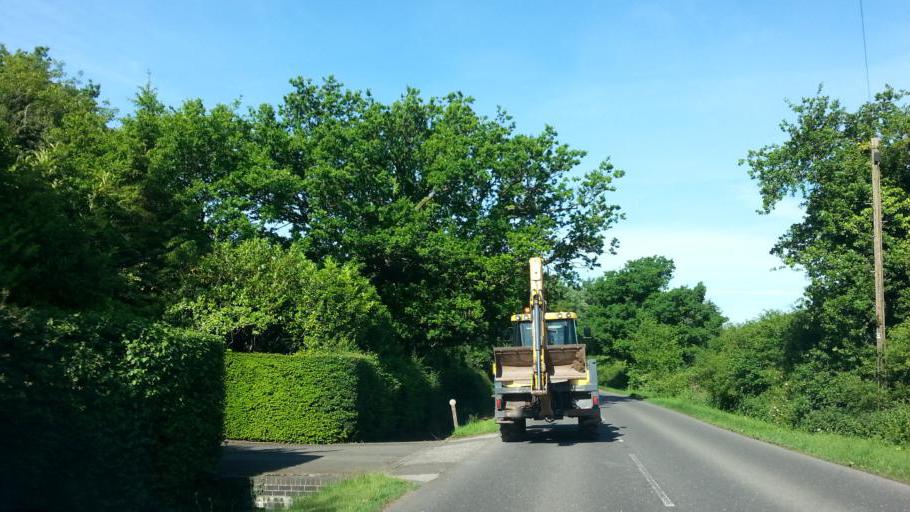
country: GB
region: England
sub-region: Nottinghamshire
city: Farnsfield
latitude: 53.0621
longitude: -1.0327
